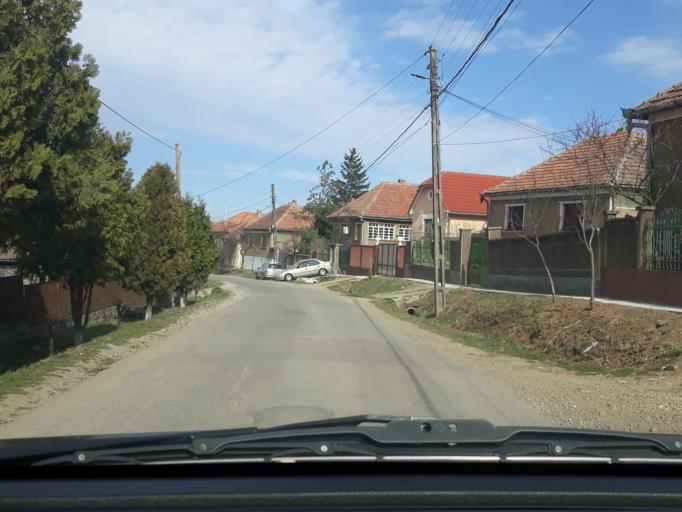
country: RO
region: Bihor
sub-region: Comuna Paleu
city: Paleu
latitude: 47.1165
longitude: 21.9580
